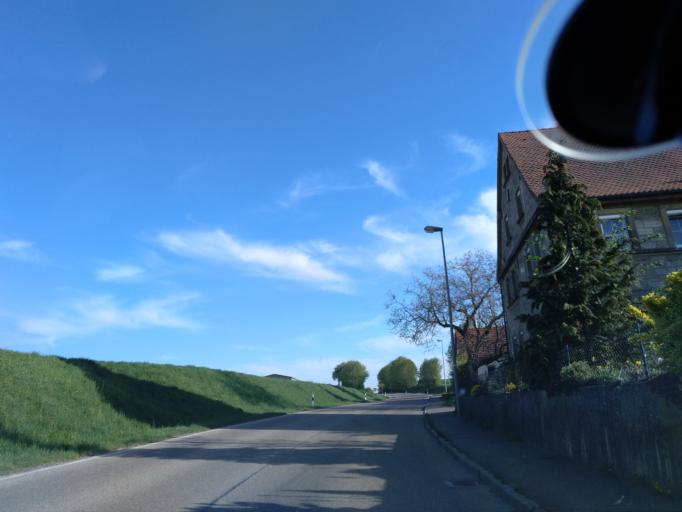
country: DE
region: Baden-Wuerttemberg
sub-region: Regierungsbezirk Stuttgart
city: Langenburg
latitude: 49.2244
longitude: 9.8482
